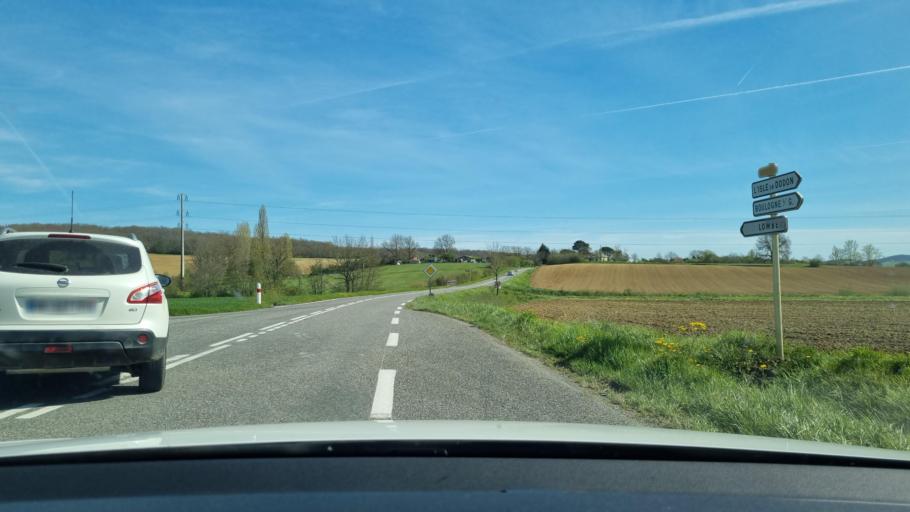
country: FR
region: Midi-Pyrenees
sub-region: Departement du Gers
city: Lombez
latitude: 43.4221
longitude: 0.8150
